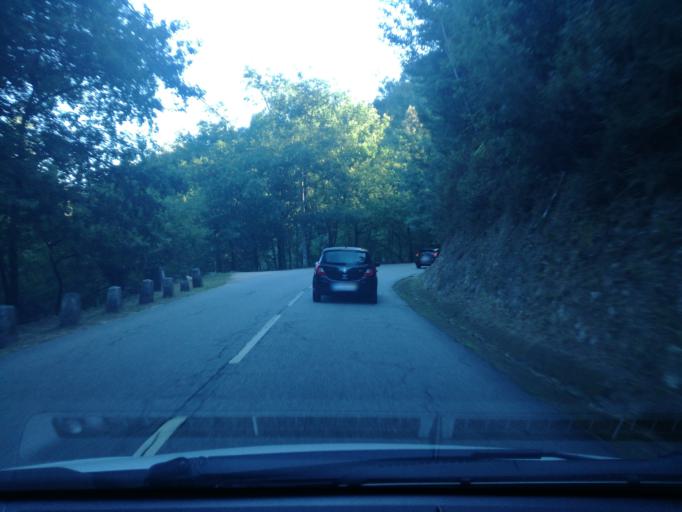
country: PT
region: Braga
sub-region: Vieira do Minho
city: Real
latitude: 41.7091
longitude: -8.1661
